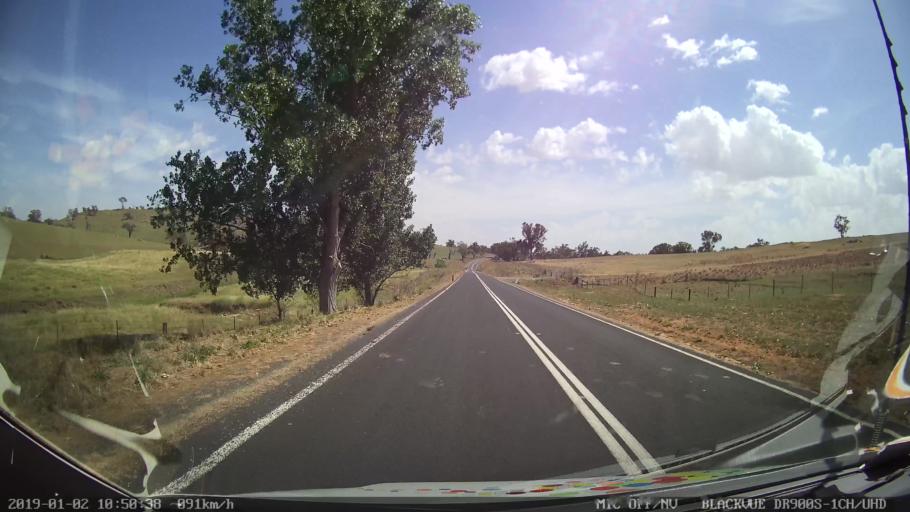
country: AU
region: New South Wales
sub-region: Cootamundra
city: Cootamundra
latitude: -34.7120
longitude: 148.2758
